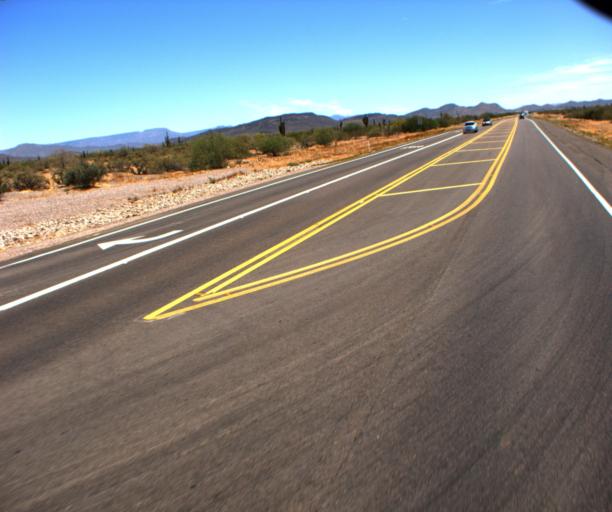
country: US
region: Arizona
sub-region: Maricopa County
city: Anthem
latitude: 33.7978
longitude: -112.2058
